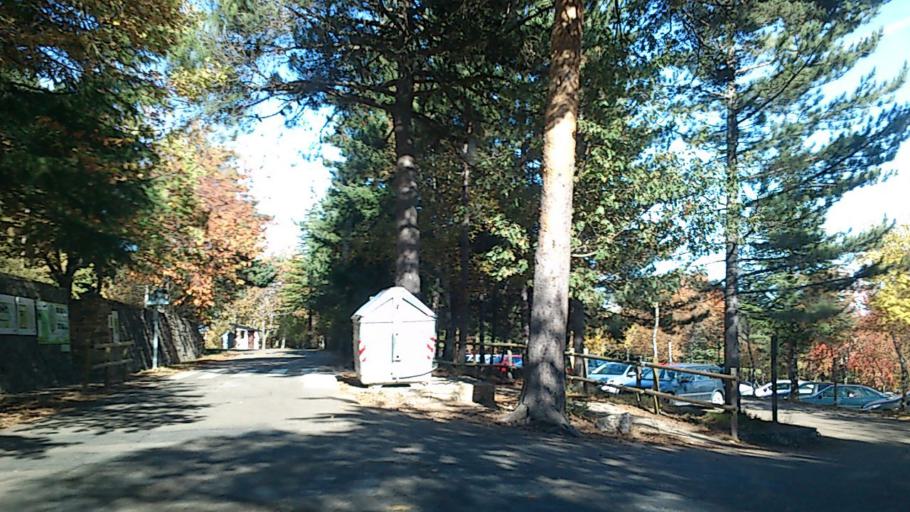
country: ES
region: Castille and Leon
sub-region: Provincia de Soria
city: Vozmediano
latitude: 41.8147
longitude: -1.8209
